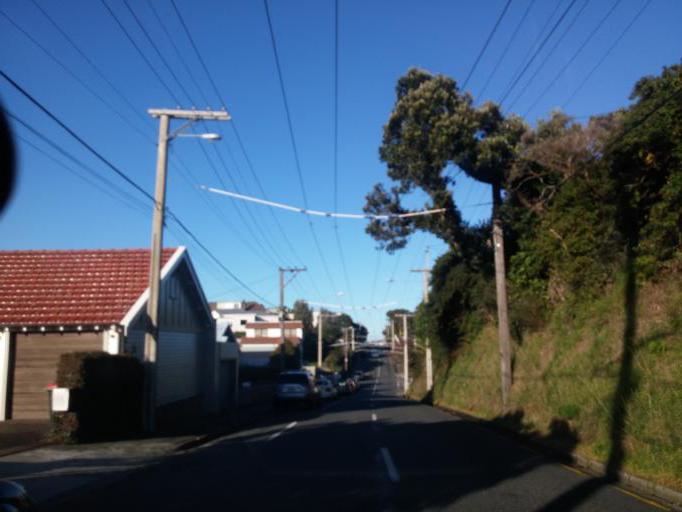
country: NZ
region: Wellington
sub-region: Wellington City
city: Brooklyn
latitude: -41.3128
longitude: 174.7658
